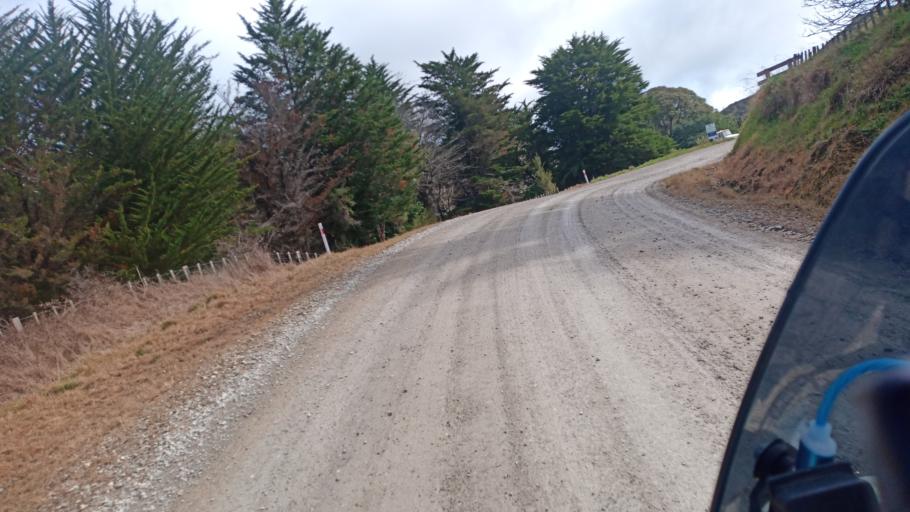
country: NZ
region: Gisborne
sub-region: Gisborne District
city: Gisborne
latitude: -38.5663
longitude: 178.1558
